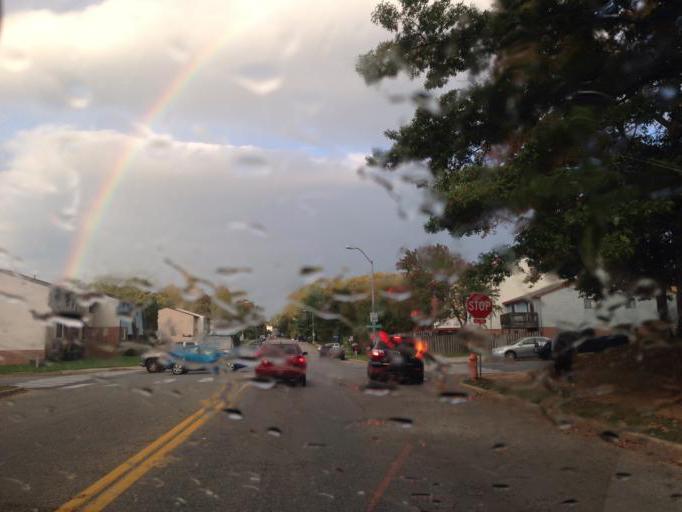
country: US
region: Maryland
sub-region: Baltimore County
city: Randallstown
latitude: 39.3869
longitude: -76.8221
